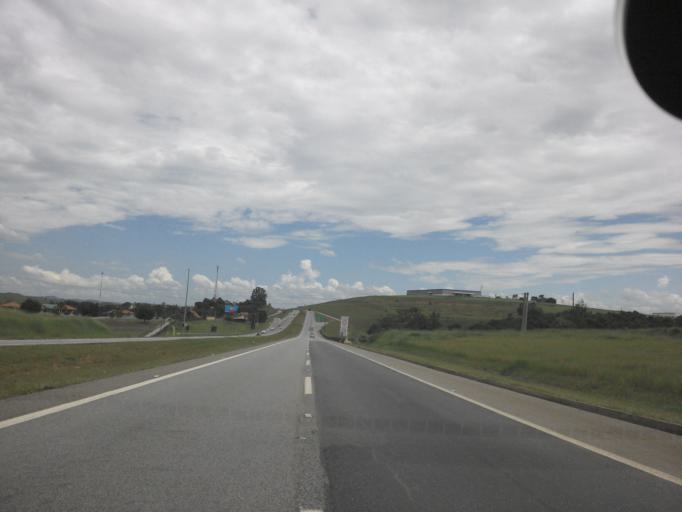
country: BR
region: Sao Paulo
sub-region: Cacapava
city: Cacapava
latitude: -23.1741
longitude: -45.7156
